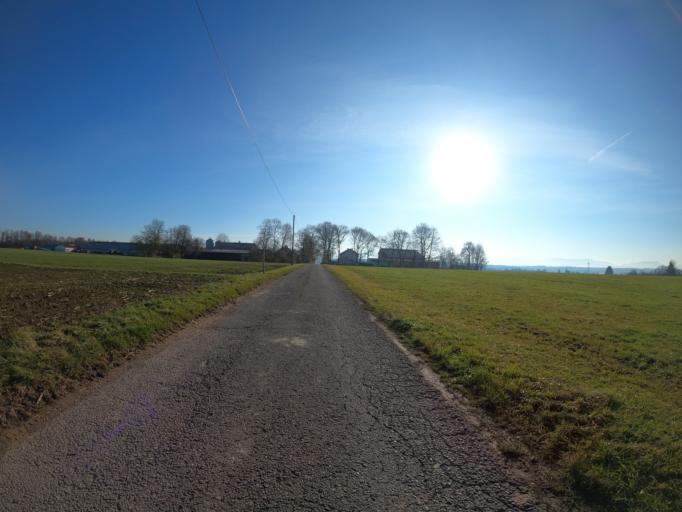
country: DE
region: Baden-Wuerttemberg
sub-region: Regierungsbezirk Stuttgart
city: Schlierbach
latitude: 48.6855
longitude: 9.5334
